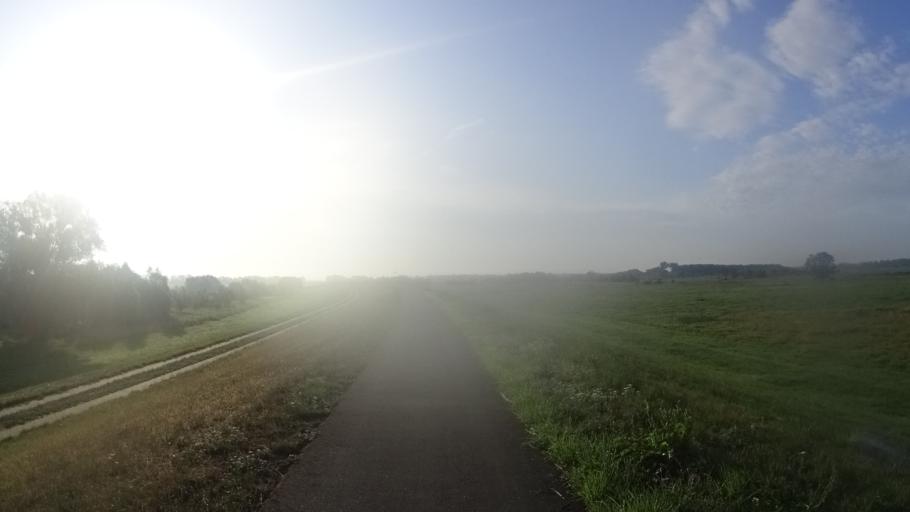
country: DE
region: Brandenburg
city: Lenzen
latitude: 53.0655
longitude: 11.4990
